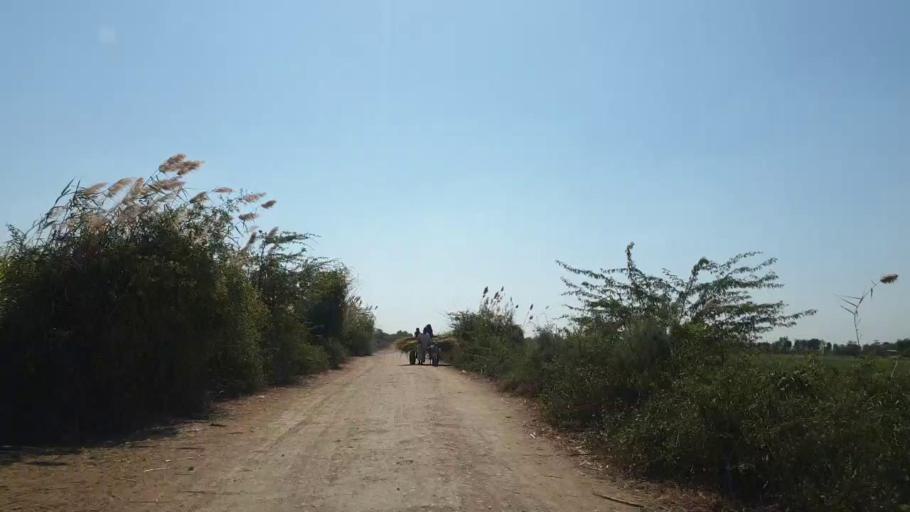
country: PK
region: Sindh
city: Mirpur Khas
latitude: 25.5951
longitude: 69.0963
